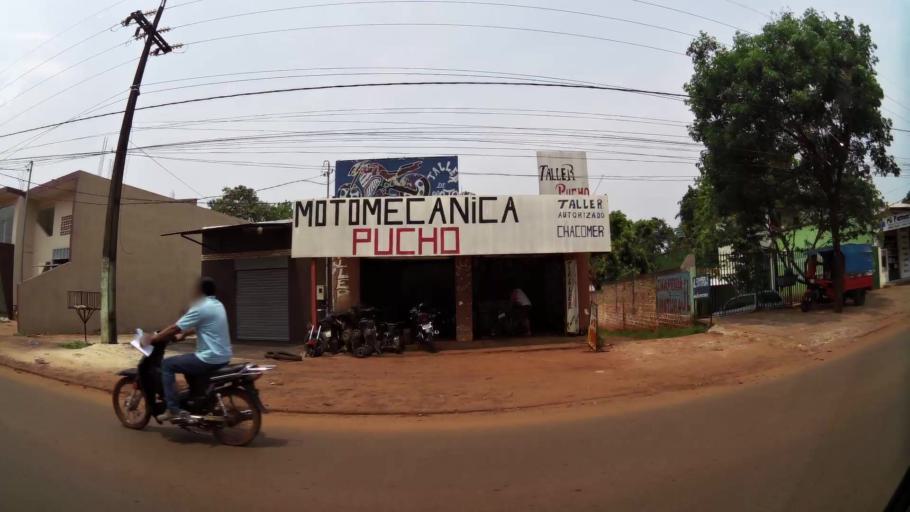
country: PY
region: Alto Parana
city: Presidente Franco
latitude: -25.5533
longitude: -54.6321
